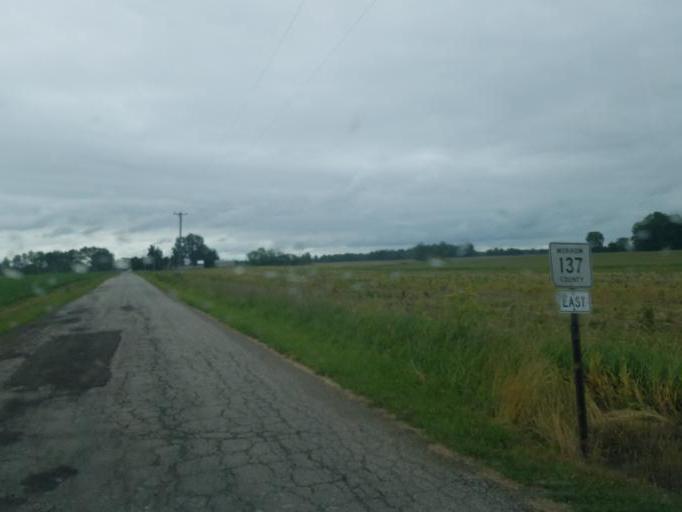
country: US
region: Ohio
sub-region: Morrow County
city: Cardington
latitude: 40.5281
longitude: -82.9004
